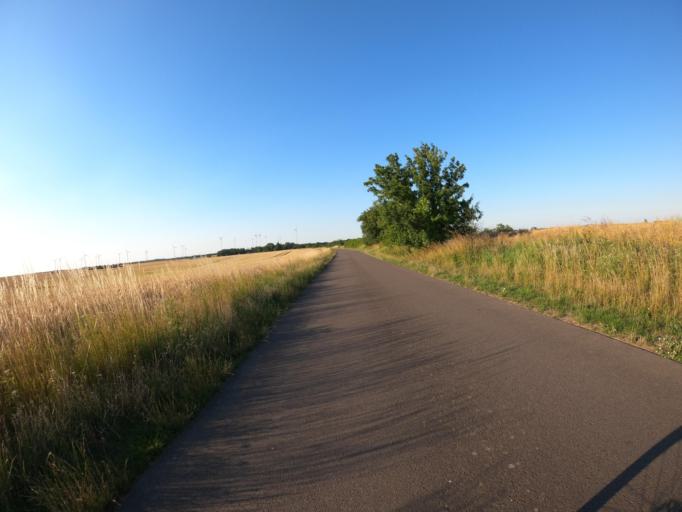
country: DE
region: Brandenburg
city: Tantow
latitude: 53.2964
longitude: 14.3814
